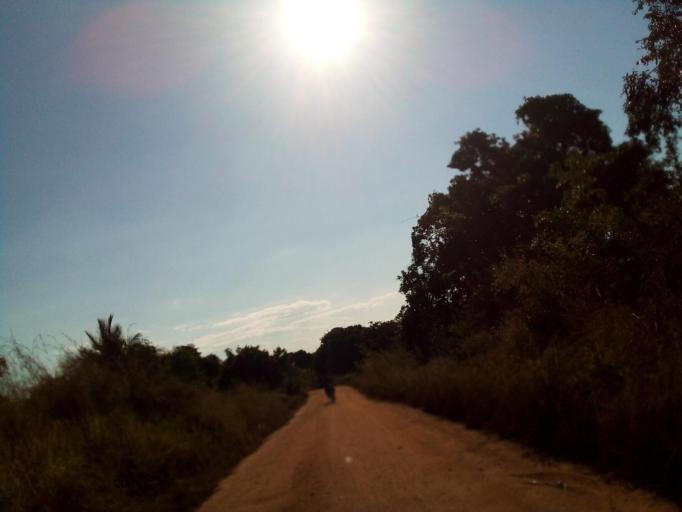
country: MZ
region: Zambezia
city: Quelimane
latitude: -17.5098
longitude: 36.5947
